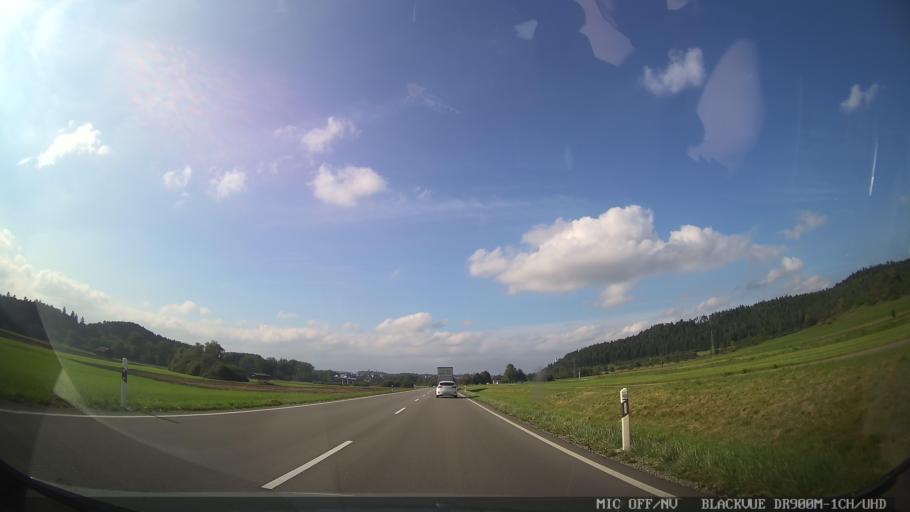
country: DE
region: Baden-Wuerttemberg
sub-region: Freiburg Region
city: Rottweil
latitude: 48.1352
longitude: 8.6595
